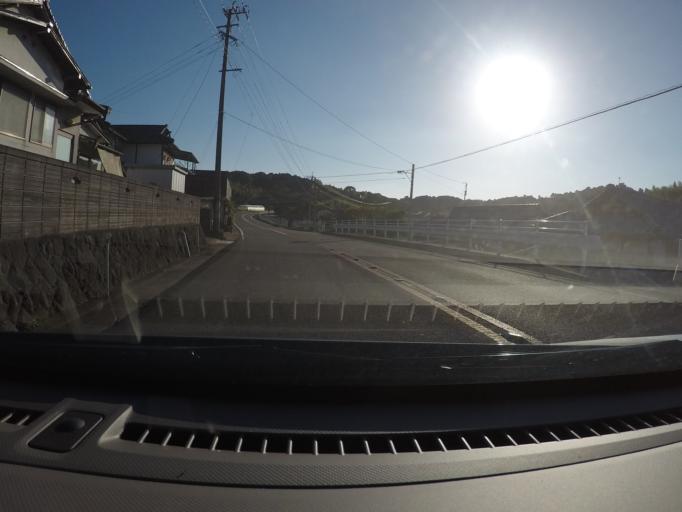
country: JP
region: Kumamoto
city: Minamata
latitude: 32.1724
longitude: 130.3813
